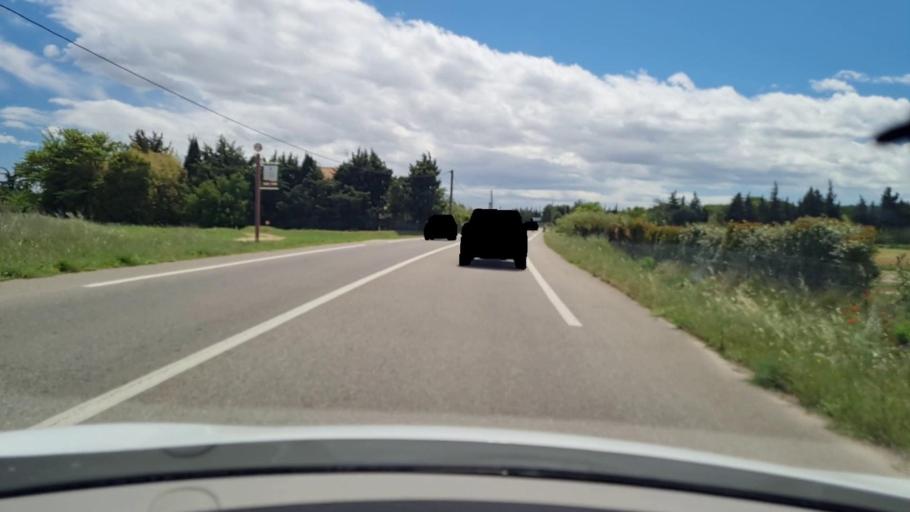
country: FR
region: Languedoc-Roussillon
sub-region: Departement du Gard
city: Vauvert
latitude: 43.6969
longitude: 4.2537
